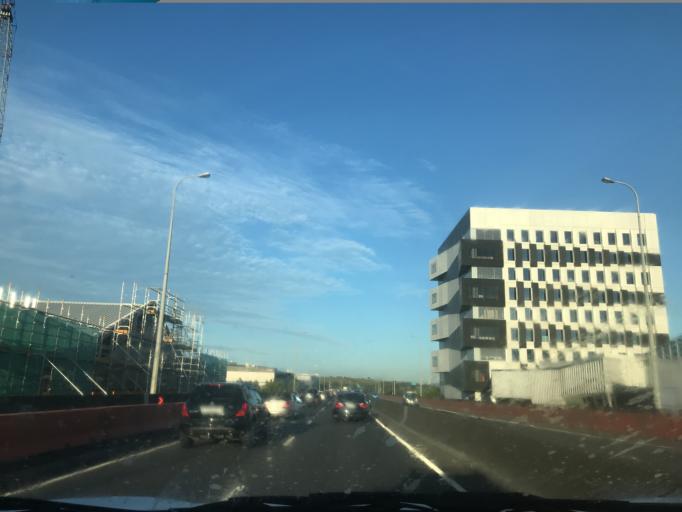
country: NZ
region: Auckland
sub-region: Auckland
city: Tamaki
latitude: -36.9152
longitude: 174.8420
